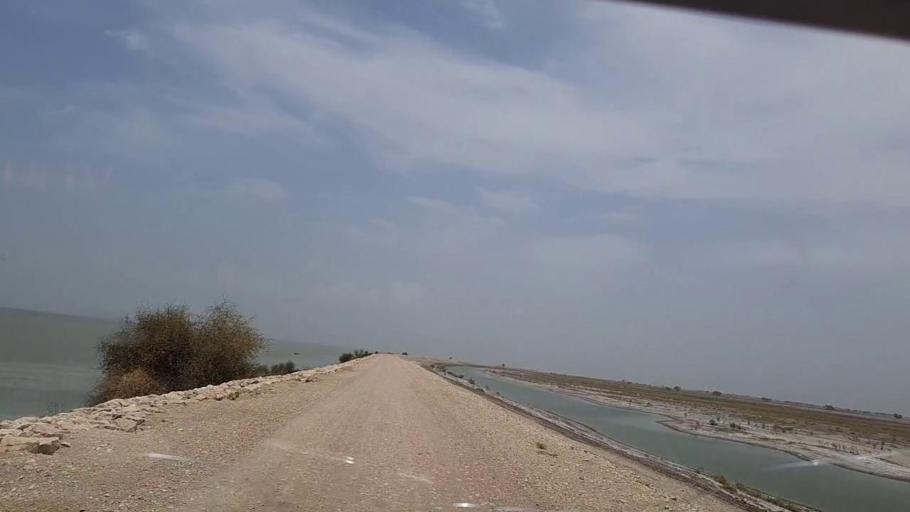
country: PK
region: Sindh
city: Sehwan
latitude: 26.4202
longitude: 67.7299
